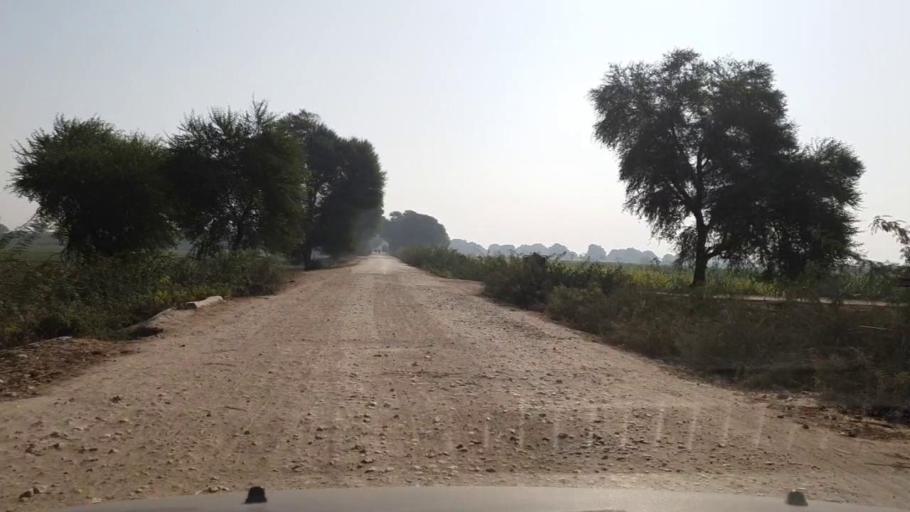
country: PK
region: Sindh
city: Matiari
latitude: 25.5474
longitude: 68.5471
